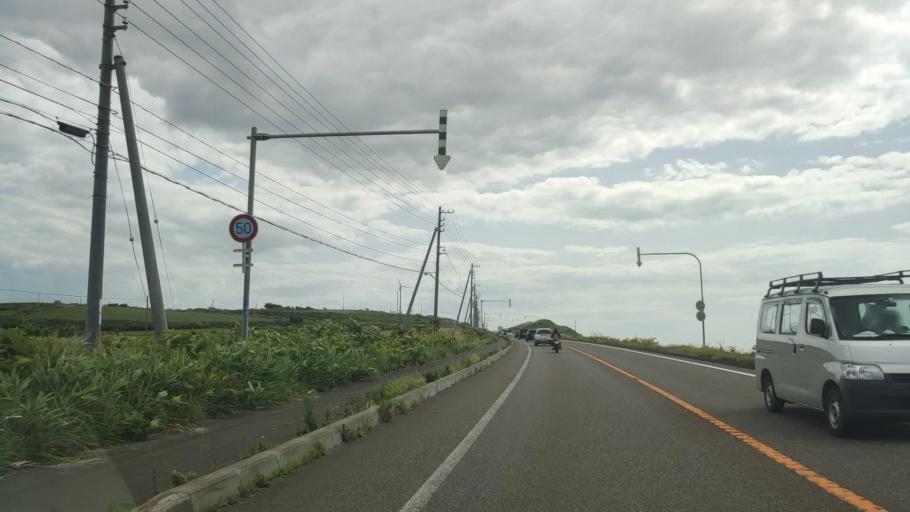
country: JP
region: Hokkaido
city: Rumoi
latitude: 44.5256
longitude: 141.7655
